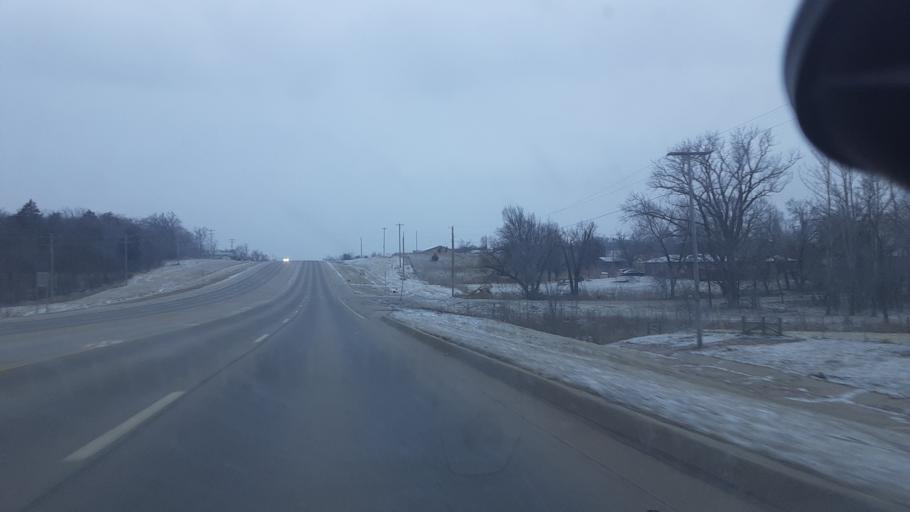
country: US
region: Oklahoma
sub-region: Payne County
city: Perkins
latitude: 35.9855
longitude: -97.0565
